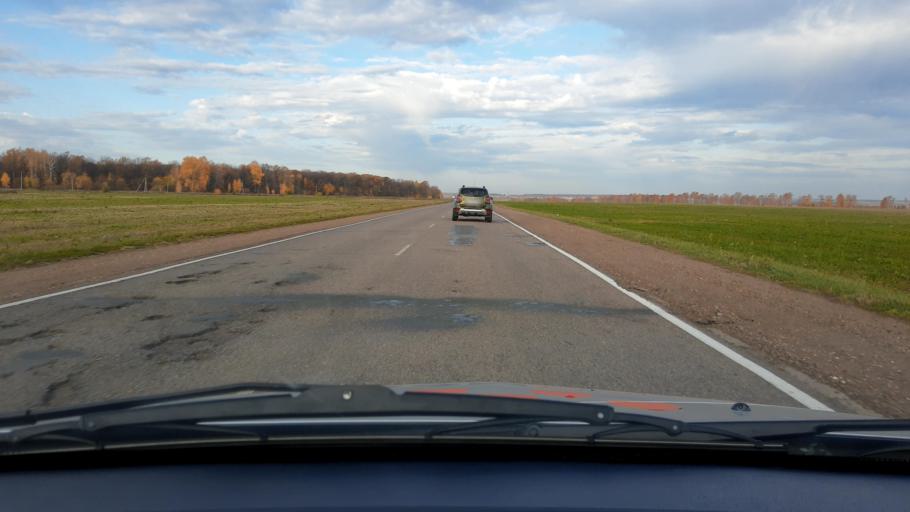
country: RU
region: Bashkortostan
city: Avdon
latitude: 54.8244
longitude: 55.6516
